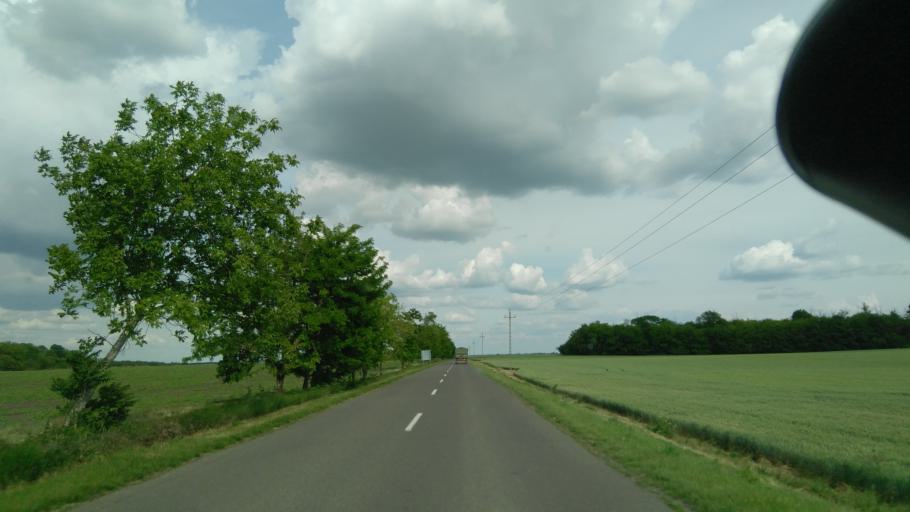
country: HU
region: Bekes
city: Mezohegyes
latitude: 46.3143
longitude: 20.8399
